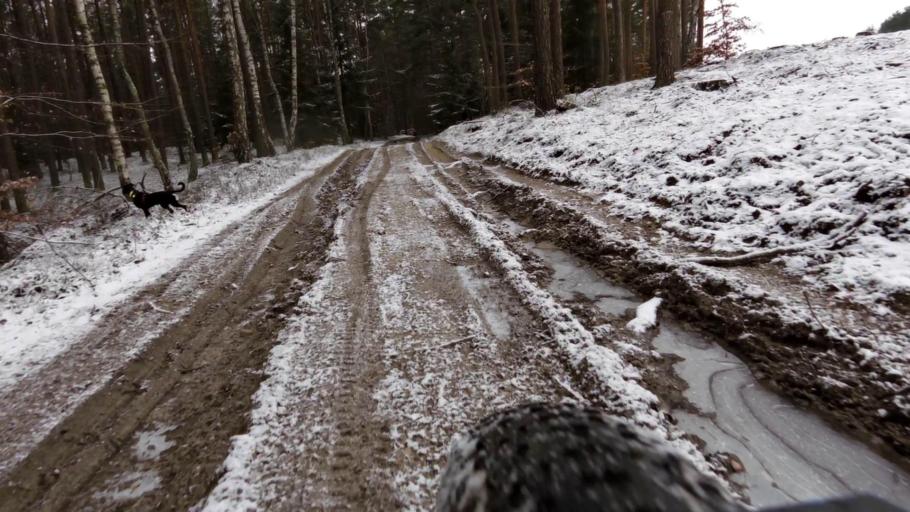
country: PL
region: West Pomeranian Voivodeship
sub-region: Powiat walecki
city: Miroslawiec
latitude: 53.3281
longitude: 16.1048
